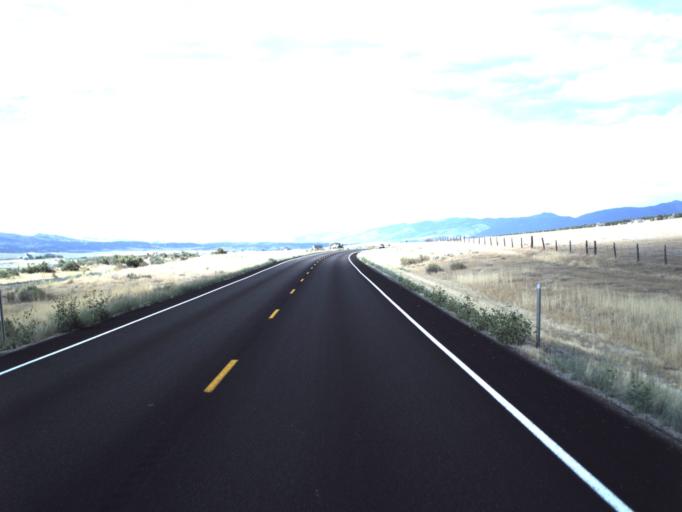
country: US
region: Utah
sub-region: Sanpete County
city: Moroni
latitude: 39.4527
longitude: -111.5427
